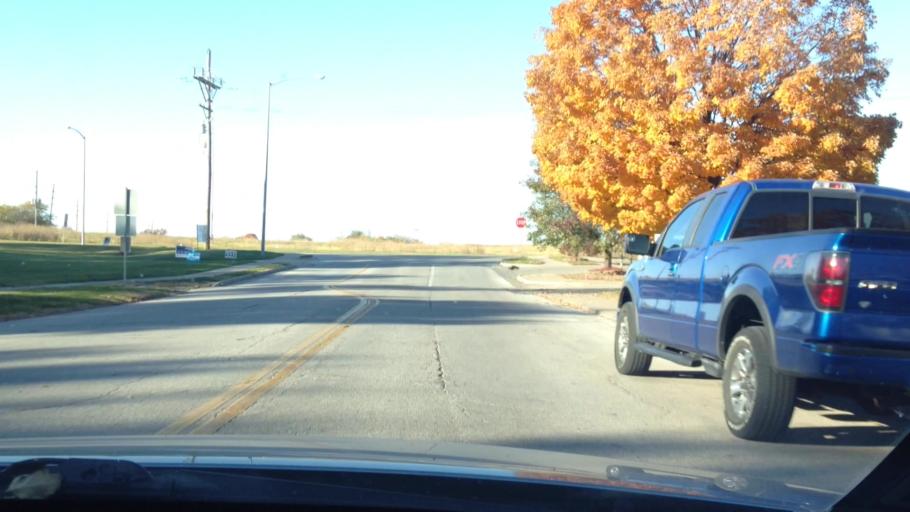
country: US
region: Kansas
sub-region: Leavenworth County
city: Leavenworth
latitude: 39.3275
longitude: -94.9234
